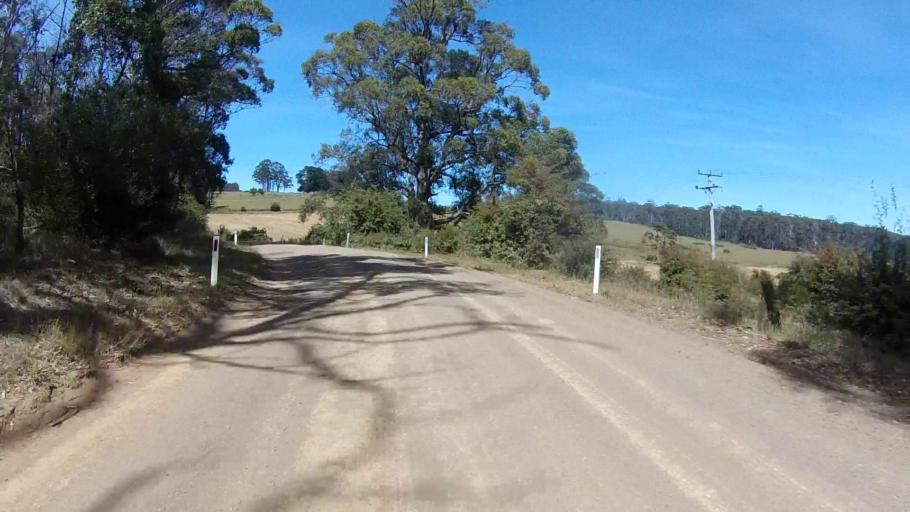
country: AU
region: Tasmania
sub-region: Sorell
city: Sorell
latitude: -42.7184
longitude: 147.7507
